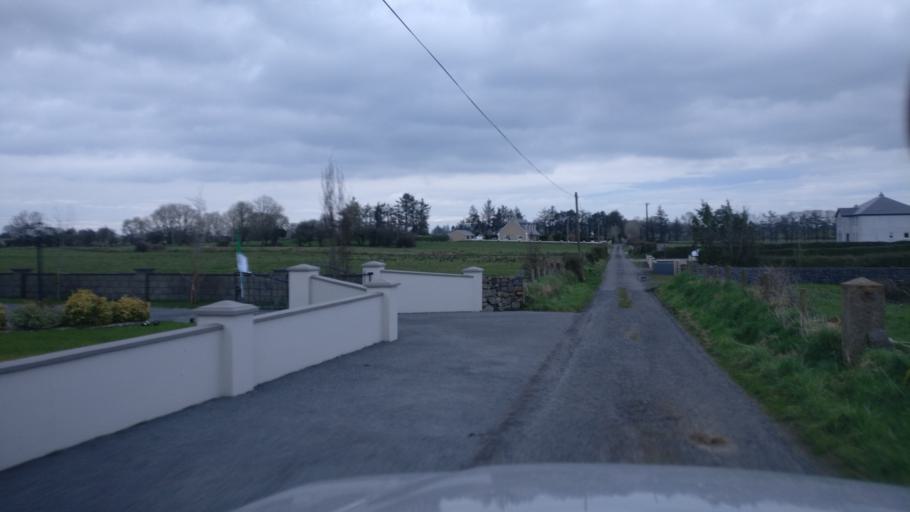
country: IE
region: Connaught
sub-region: County Galway
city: Loughrea
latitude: 53.2606
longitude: -8.4905
